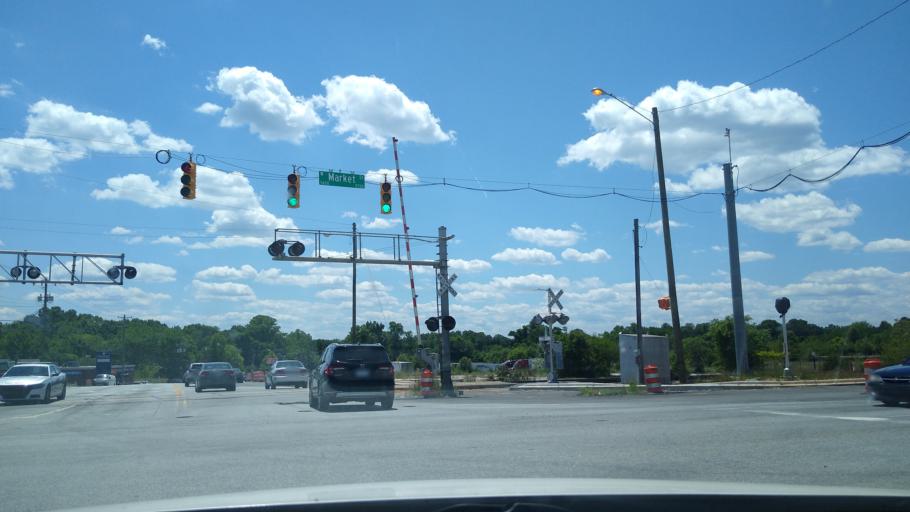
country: US
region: North Carolina
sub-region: Guilford County
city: Jamestown
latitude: 36.0768
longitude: -79.8976
